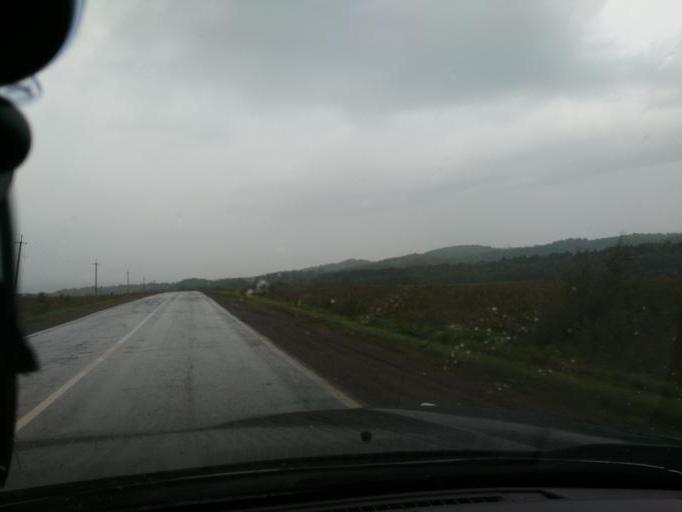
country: RU
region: Perm
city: Barda
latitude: 56.9372
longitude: 55.6551
